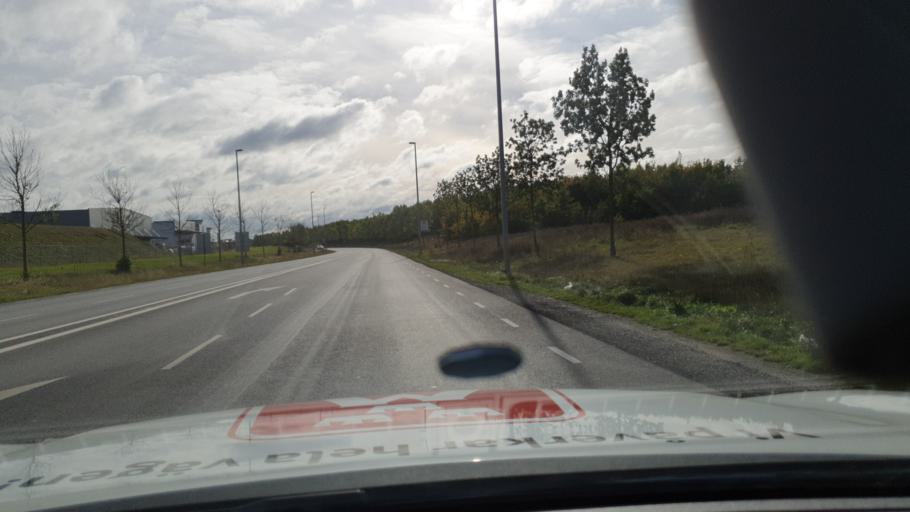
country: SE
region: Skane
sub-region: Malmo
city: Tygelsjo
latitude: 55.5595
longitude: 13.0269
